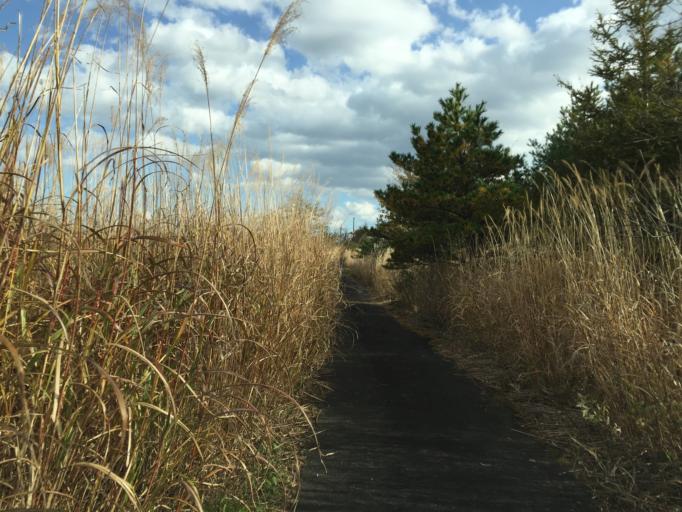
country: JP
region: Fukushima
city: Fukushima-shi
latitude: 37.7349
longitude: 140.3138
